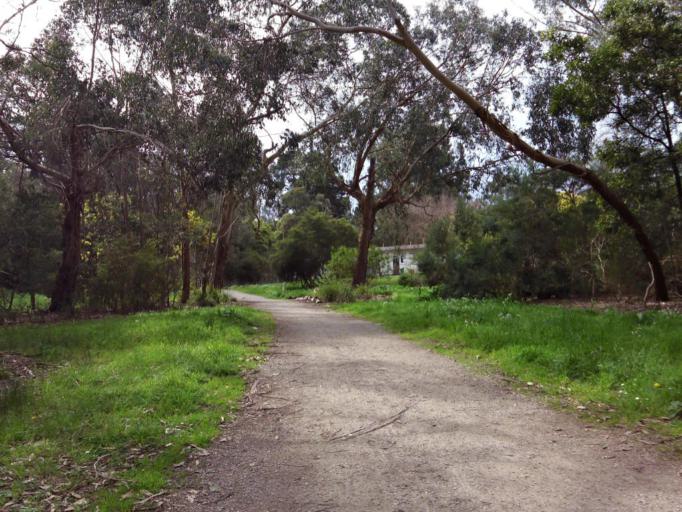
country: AU
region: Victoria
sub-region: Maroondah
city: Ringwood East
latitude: -37.8055
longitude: 145.2394
